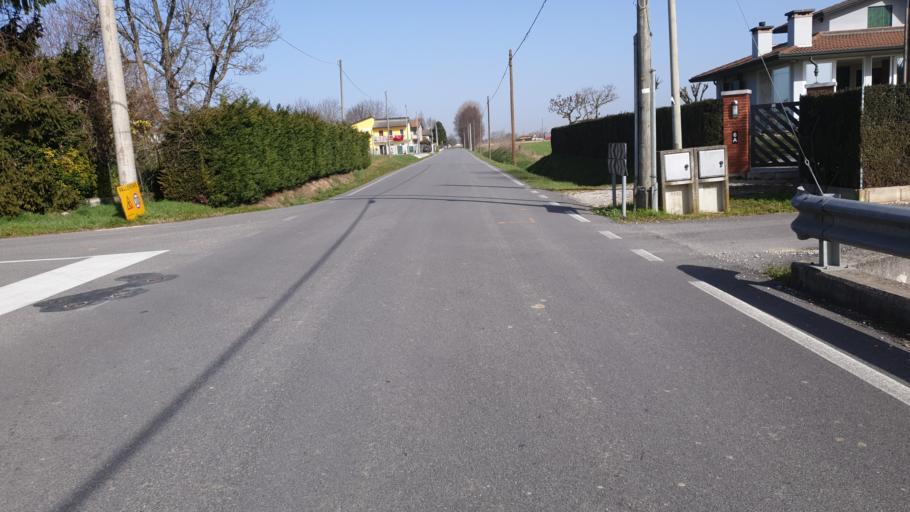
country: IT
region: Veneto
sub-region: Provincia di Padova
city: Cavino
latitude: 45.5050
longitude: 11.8891
